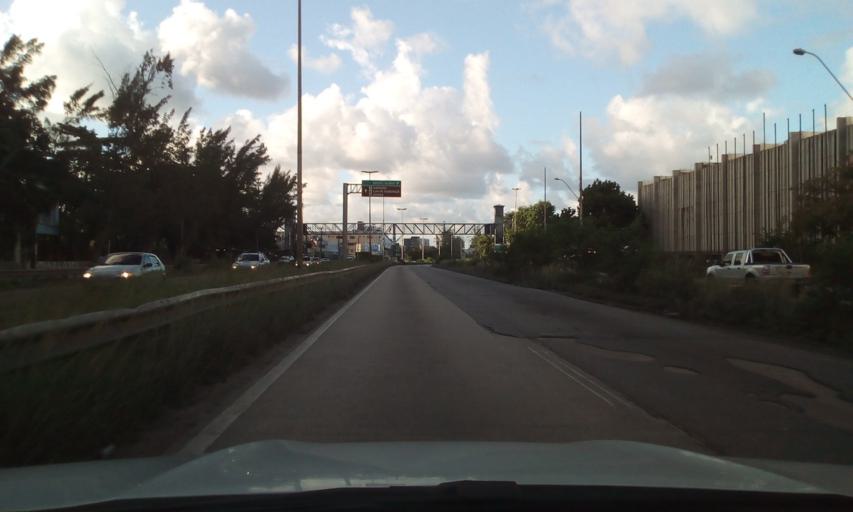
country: BR
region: Pernambuco
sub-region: Recife
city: Recife
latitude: -8.0483
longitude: -34.9453
